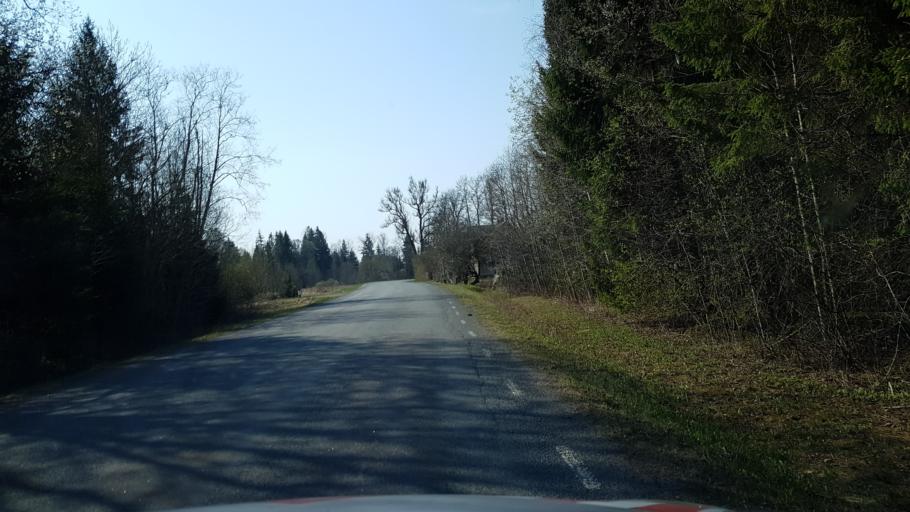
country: EE
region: Raplamaa
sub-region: Maerjamaa vald
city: Marjamaa
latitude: 58.8716
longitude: 24.3745
